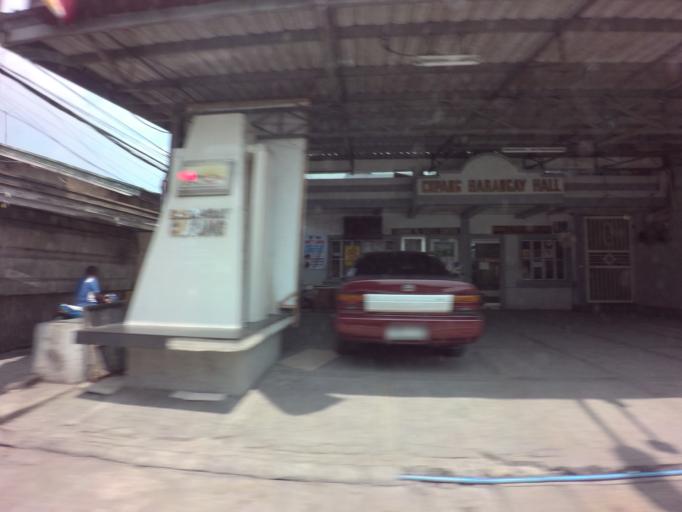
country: PH
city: Sambayanihan People's Village
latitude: 14.4391
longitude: 121.0504
